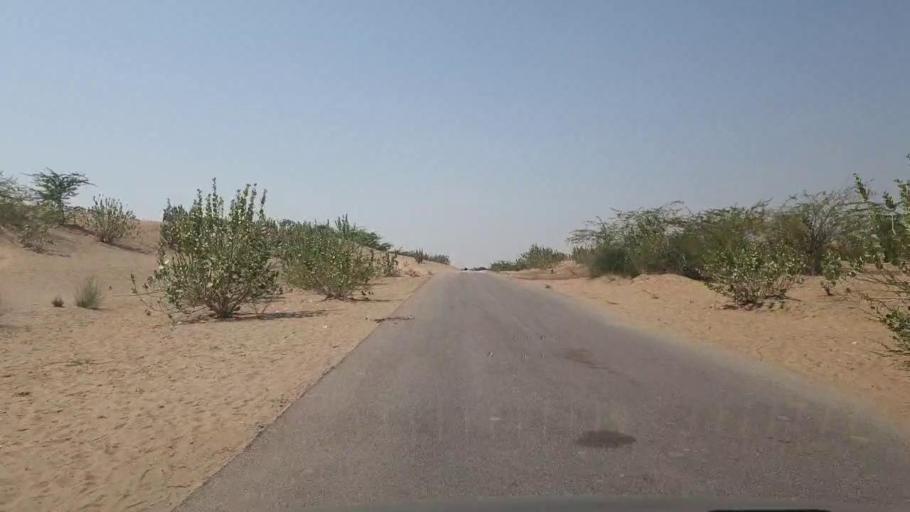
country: PK
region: Sindh
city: Chor
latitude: 25.5763
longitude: 70.1900
